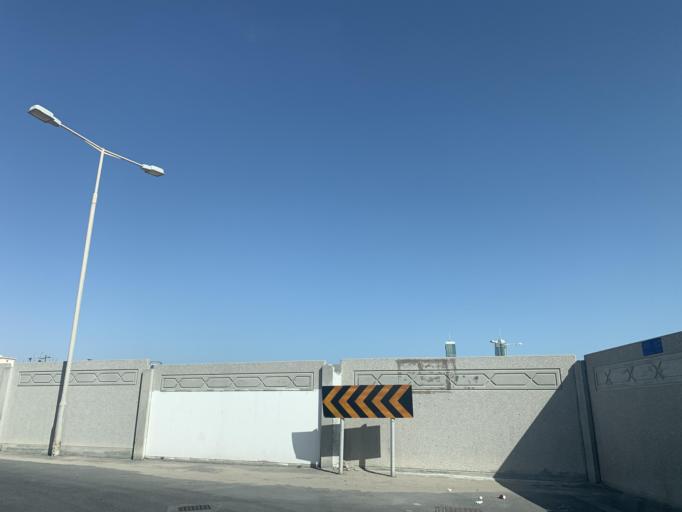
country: BH
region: Manama
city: Manama
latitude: 26.2227
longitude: 50.5795
